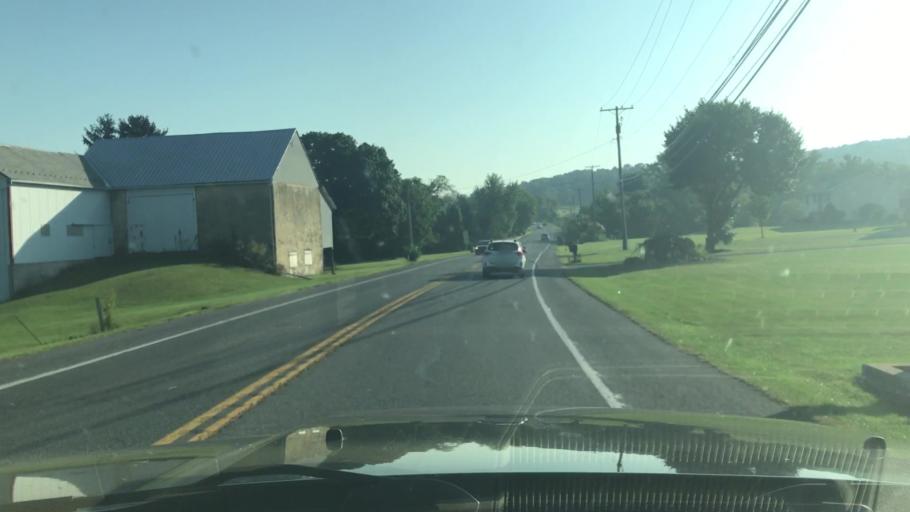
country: US
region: Pennsylvania
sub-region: Berks County
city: Topton
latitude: 40.4892
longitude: -75.7253
